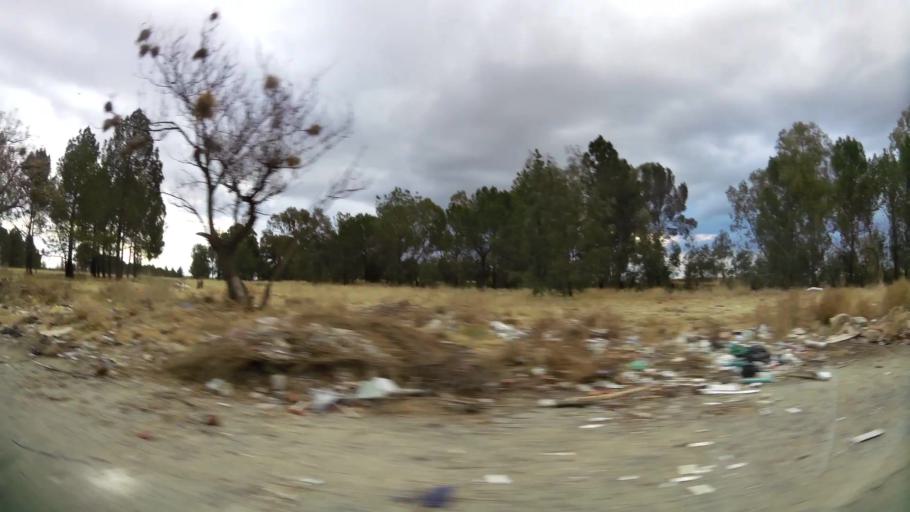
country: ZA
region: Orange Free State
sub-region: Lejweleputswa District Municipality
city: Welkom
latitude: -27.9647
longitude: 26.7032
